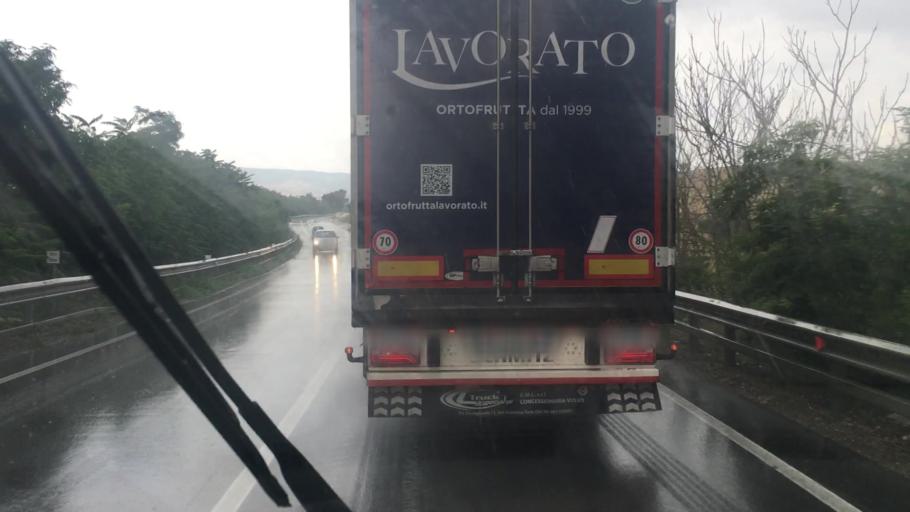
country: IT
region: Basilicate
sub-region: Provincia di Matera
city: Matera
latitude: 40.6283
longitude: 16.5906
